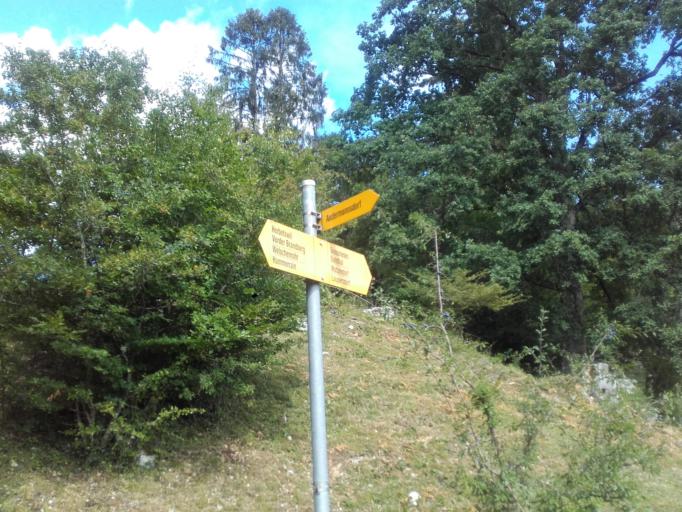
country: CH
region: Solothurn
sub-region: Bezirk Thal
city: Matzendorf
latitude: 47.3077
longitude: 7.5889
